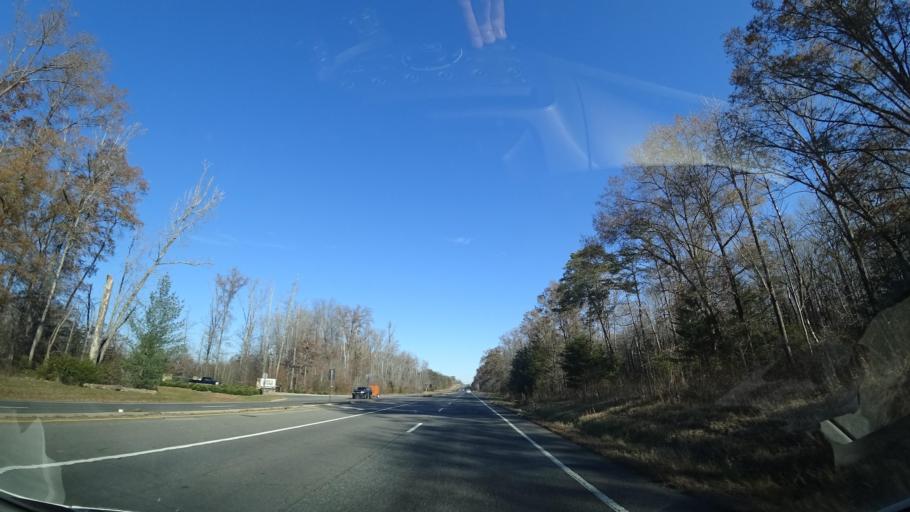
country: US
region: Virginia
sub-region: Spotsylvania County
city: Spotsylvania Courthouse
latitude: 38.1738
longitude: -77.5181
